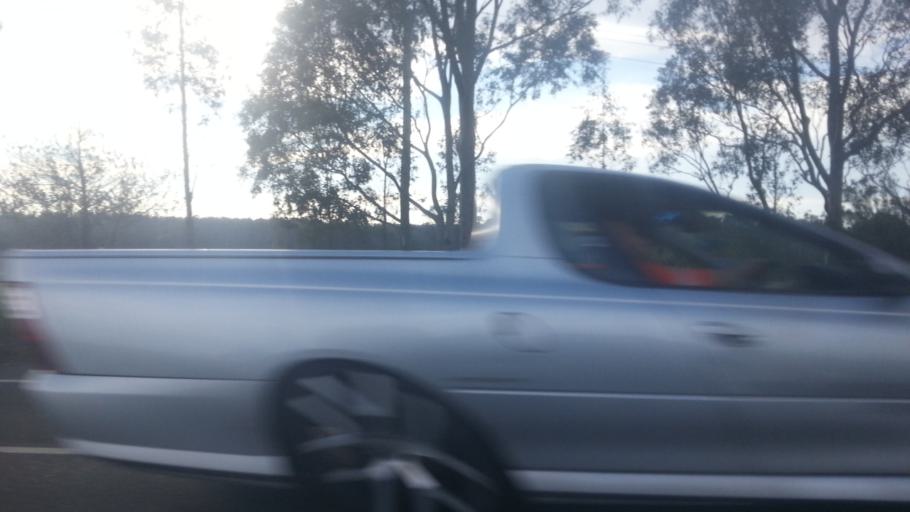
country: AU
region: New South Wales
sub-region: Campbelltown Municipality
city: Glen Alpine
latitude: -34.1262
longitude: 150.7923
